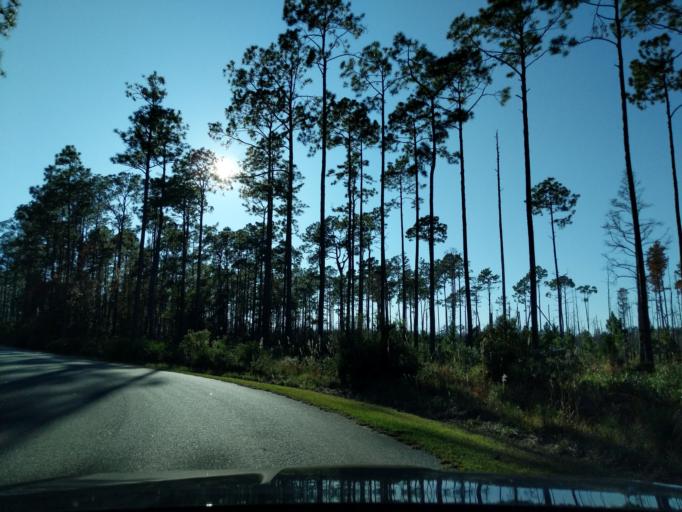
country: US
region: Georgia
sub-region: Charlton County
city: Folkston
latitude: 30.7116
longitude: -82.1435
